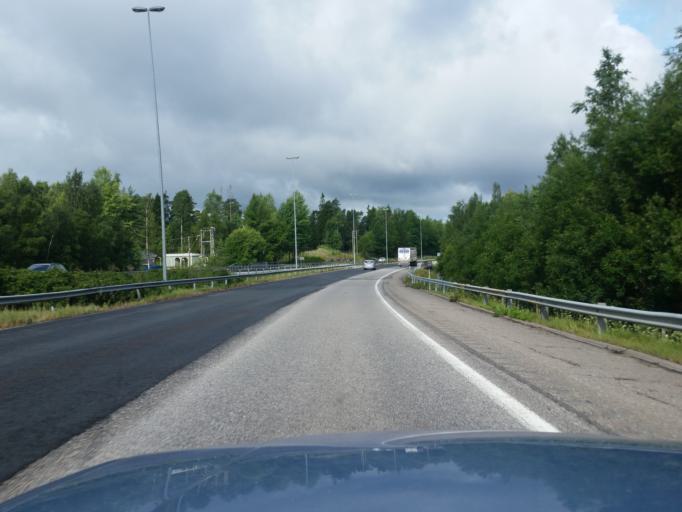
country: FI
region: Uusimaa
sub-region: Helsinki
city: Kirkkonummi
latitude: 60.2556
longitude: 24.5077
